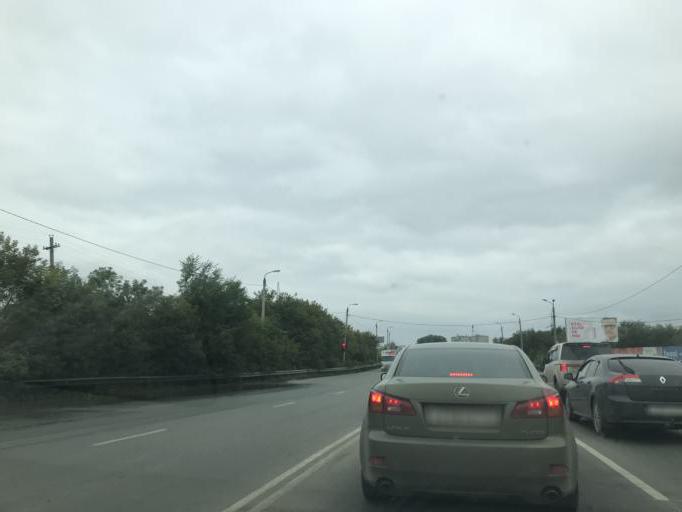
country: RU
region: Chelyabinsk
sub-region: Gorod Chelyabinsk
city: Chelyabinsk
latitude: 55.1655
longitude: 61.4283
